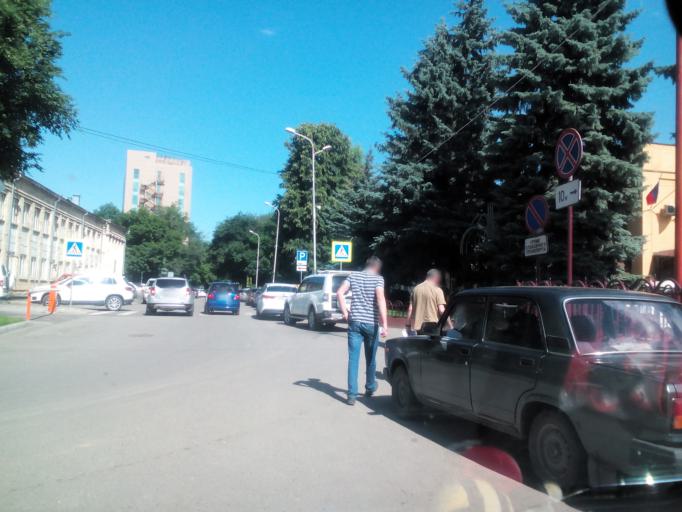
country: RU
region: Stavropol'skiy
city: Pyatigorsk
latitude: 44.0345
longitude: 43.0619
